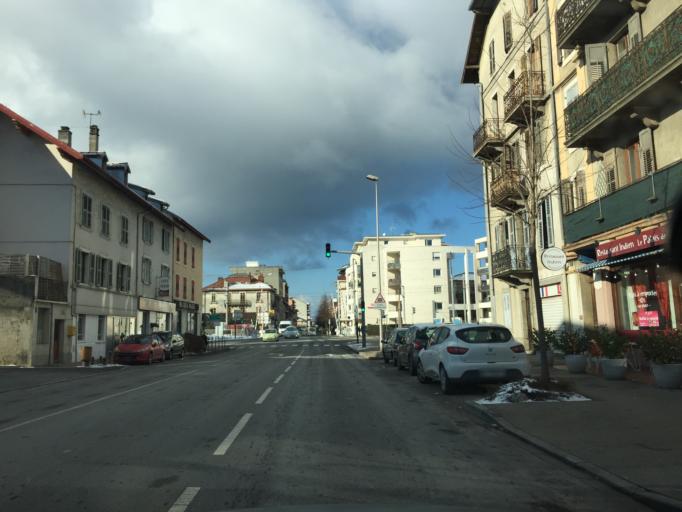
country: FR
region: Rhone-Alpes
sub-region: Departement de la Haute-Savoie
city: Thonon-les-Bains
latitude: 46.3705
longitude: 6.4858
